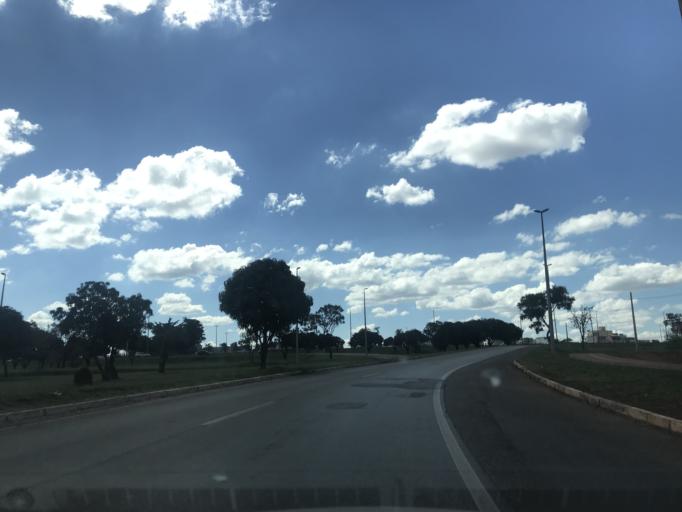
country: BR
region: Federal District
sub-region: Brasilia
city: Brasilia
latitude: -15.7879
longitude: -47.9970
